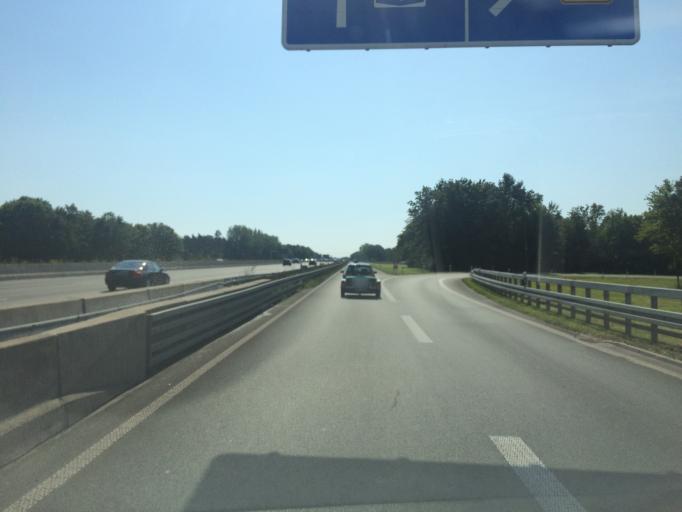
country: DE
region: North Rhine-Westphalia
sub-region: Regierungsbezirk Munster
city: Muenster
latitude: 51.9153
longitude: 7.5602
